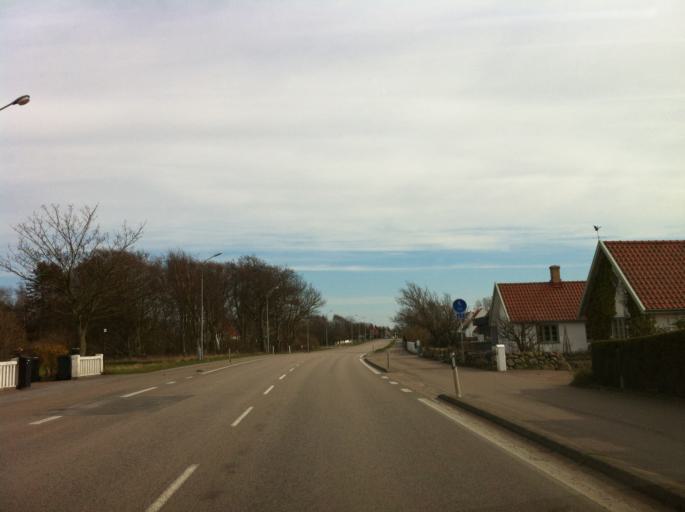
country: SE
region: Skane
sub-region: Hoganas Kommun
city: Hoganas
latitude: 56.2177
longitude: 12.5465
